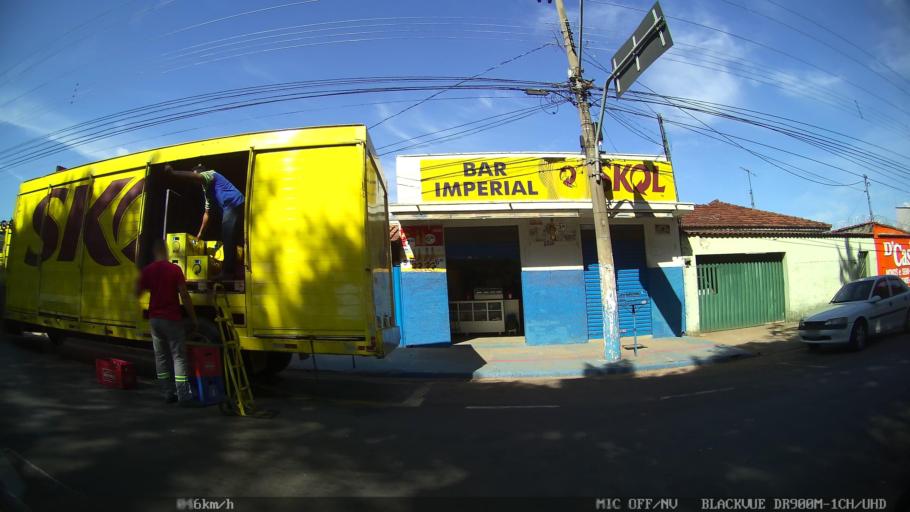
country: BR
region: Sao Paulo
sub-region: Franca
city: Franca
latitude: -20.5107
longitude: -47.4006
